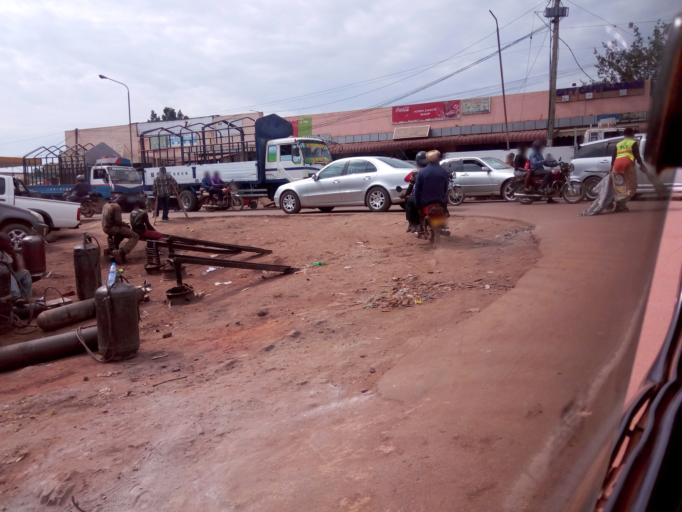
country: UG
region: Central Region
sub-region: Kampala District
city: Kampala
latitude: 0.3086
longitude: 32.5694
